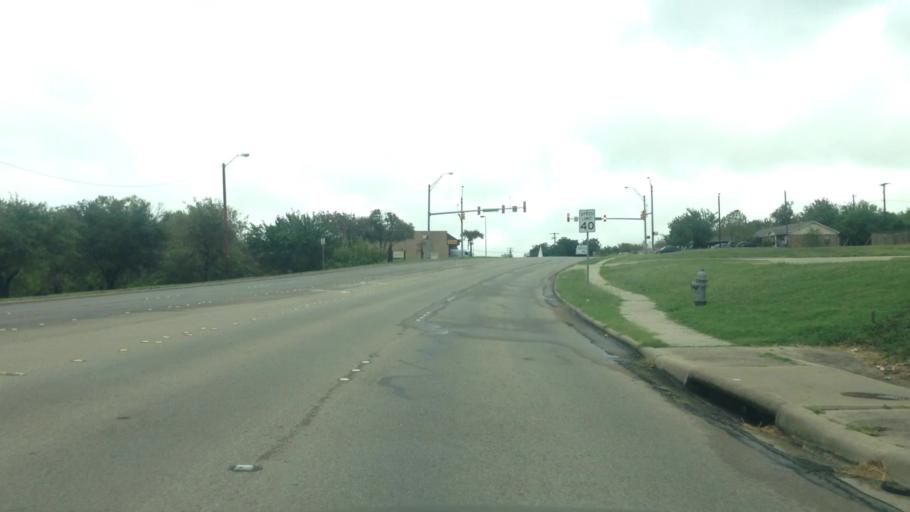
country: US
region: Texas
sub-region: Tarrant County
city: White Settlement
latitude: 32.7660
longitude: -97.4647
